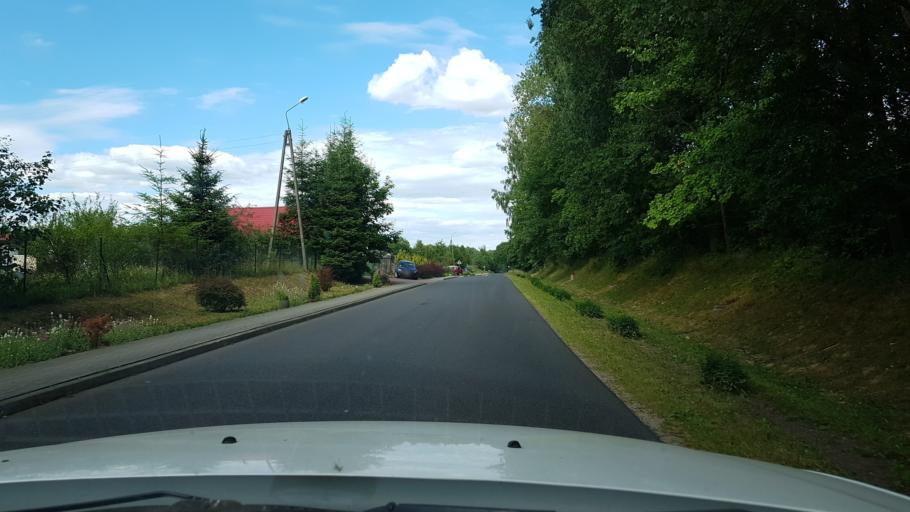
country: PL
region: West Pomeranian Voivodeship
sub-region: Powiat drawski
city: Kalisz Pomorski
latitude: 53.3760
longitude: 15.9389
